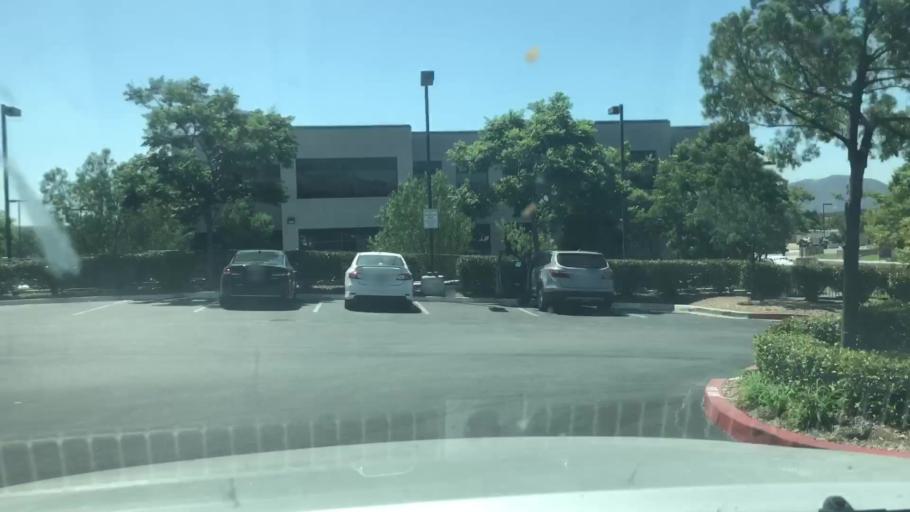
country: US
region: California
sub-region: Riverside County
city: Murrieta
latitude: 33.5920
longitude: -117.2363
